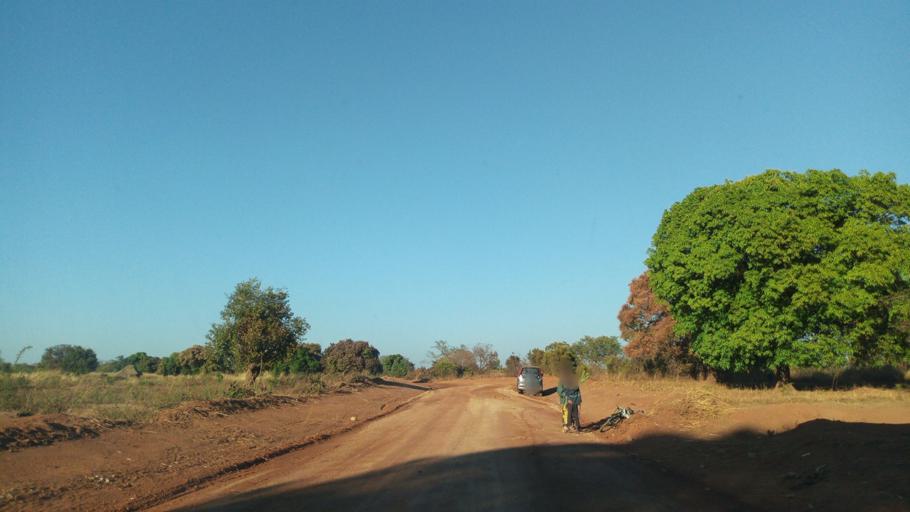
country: ZM
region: Luapula
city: Mwense
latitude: -10.4222
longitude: 28.6024
